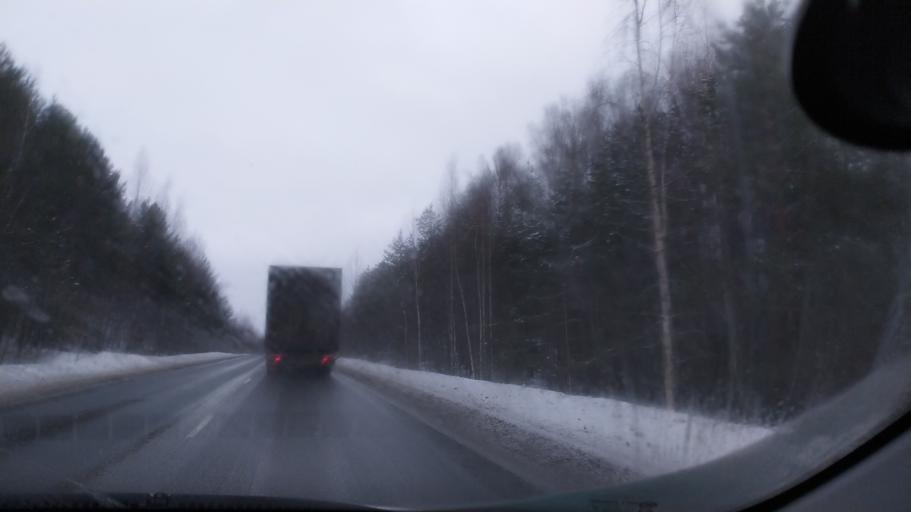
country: RU
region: Chuvashia
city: Mariinskiy Posad
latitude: 56.1817
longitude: 47.8586
